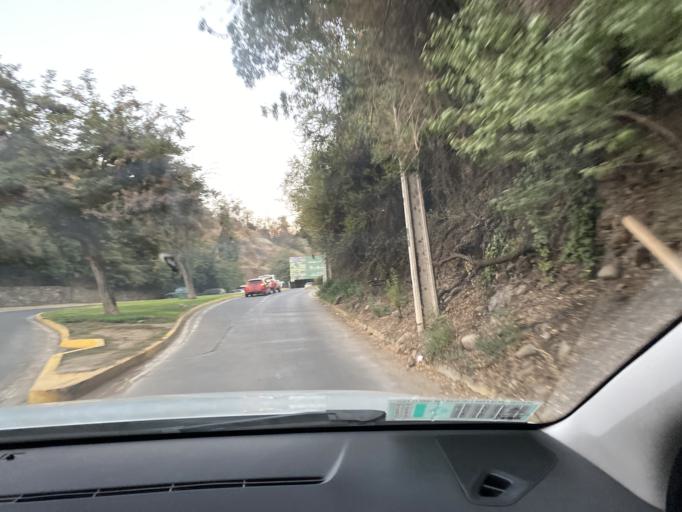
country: CL
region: Santiago Metropolitan
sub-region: Provincia de Santiago
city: Villa Presidente Frei, Nunoa, Santiago, Chile
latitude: -33.3617
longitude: -70.4931
